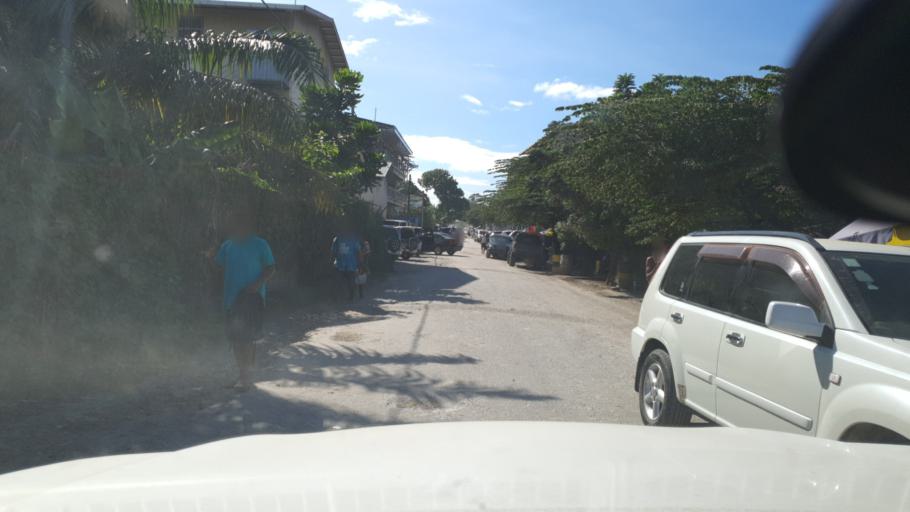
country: SB
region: Guadalcanal
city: Honiara
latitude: -9.4331
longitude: 159.9824
